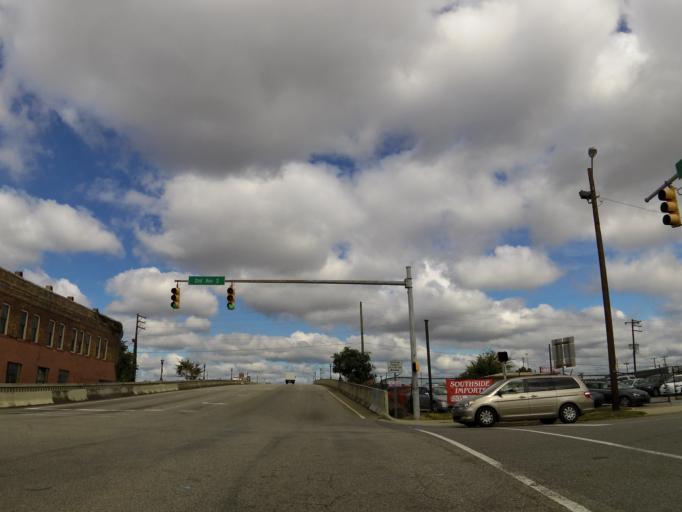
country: US
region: Alabama
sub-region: Jefferson County
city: Birmingham
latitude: 33.5134
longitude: -86.7976
